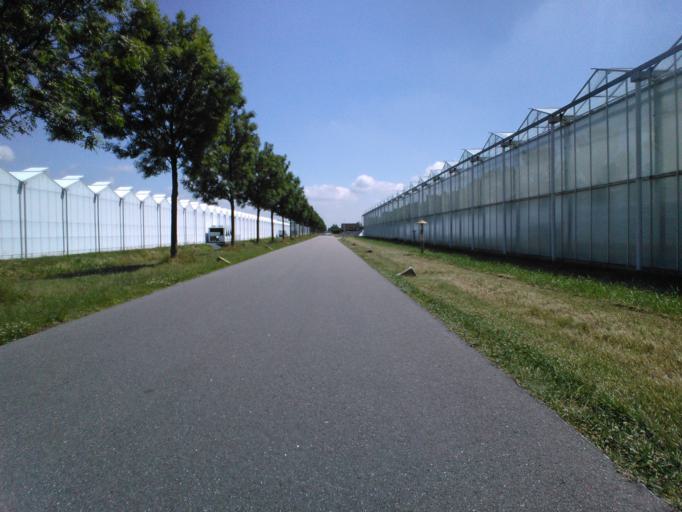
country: NL
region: South Holland
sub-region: Gemeente Westland
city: De Lier
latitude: 51.9741
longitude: 4.2773
